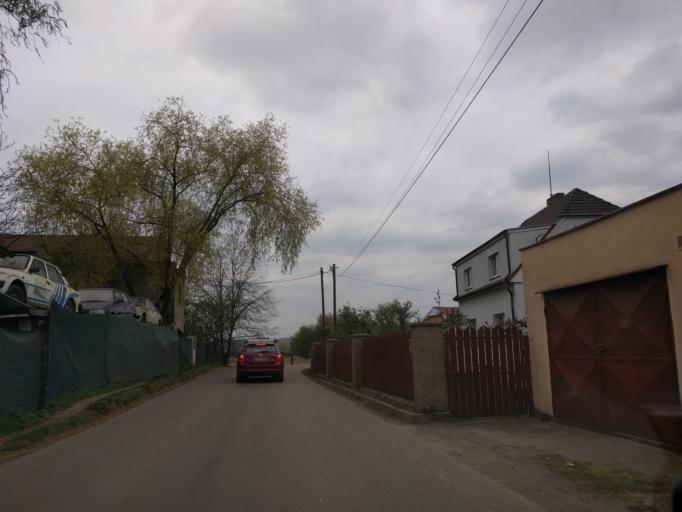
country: CZ
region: Central Bohemia
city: Revnice
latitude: 49.9170
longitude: 14.2498
